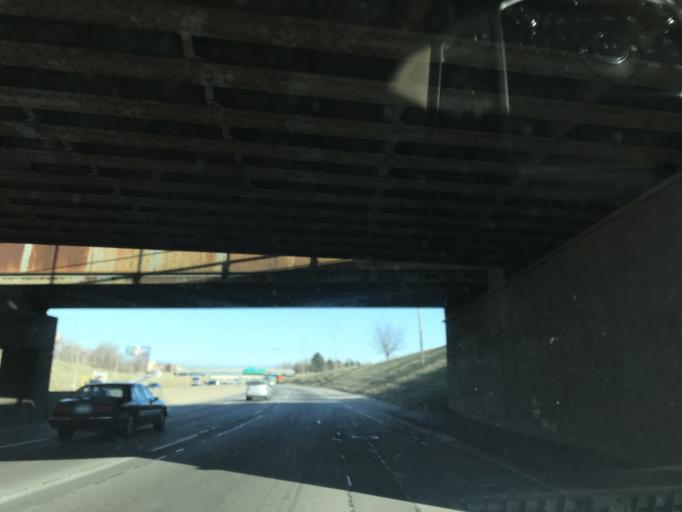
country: US
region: Michigan
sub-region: Wayne County
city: Grosse Pointe Park
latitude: 42.3934
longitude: -82.9920
